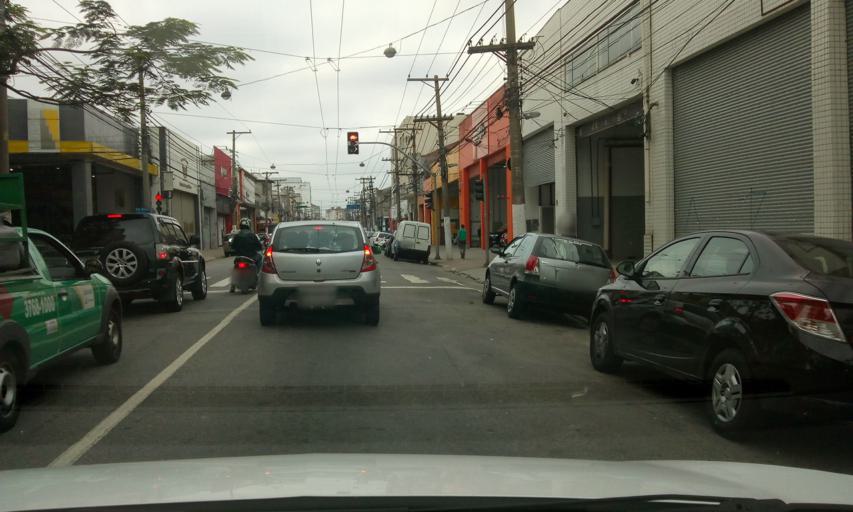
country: BR
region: Sao Paulo
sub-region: Sao Paulo
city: Sao Paulo
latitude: -23.5494
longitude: -46.6181
